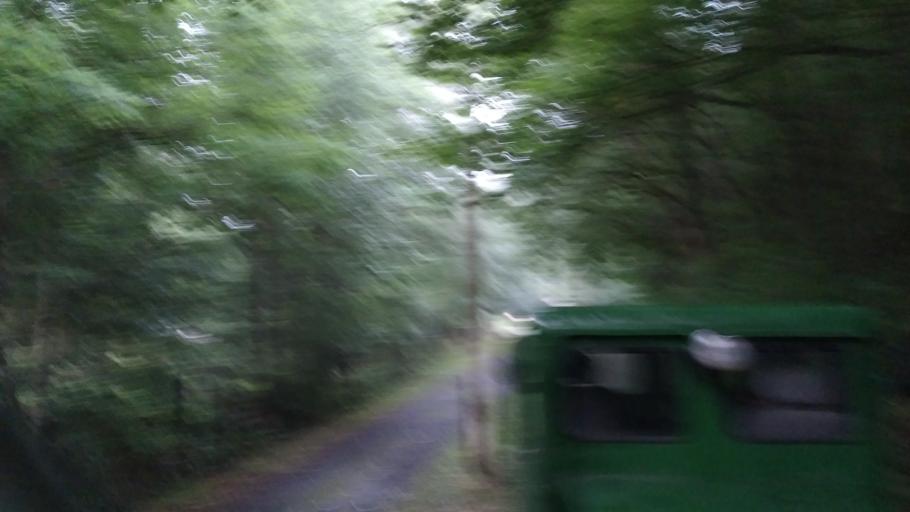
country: HU
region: Pest
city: Szob
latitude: 47.9307
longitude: 18.8397
